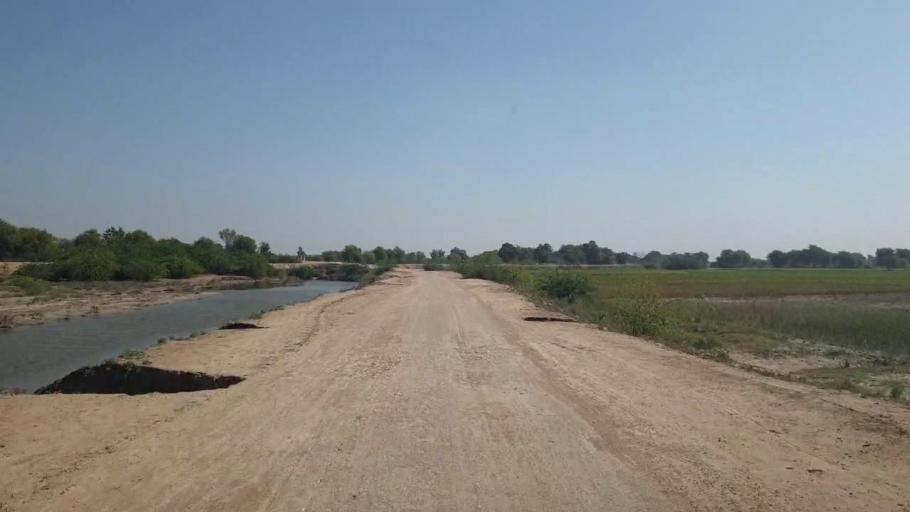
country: PK
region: Sindh
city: Talhar
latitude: 24.7916
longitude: 68.8019
